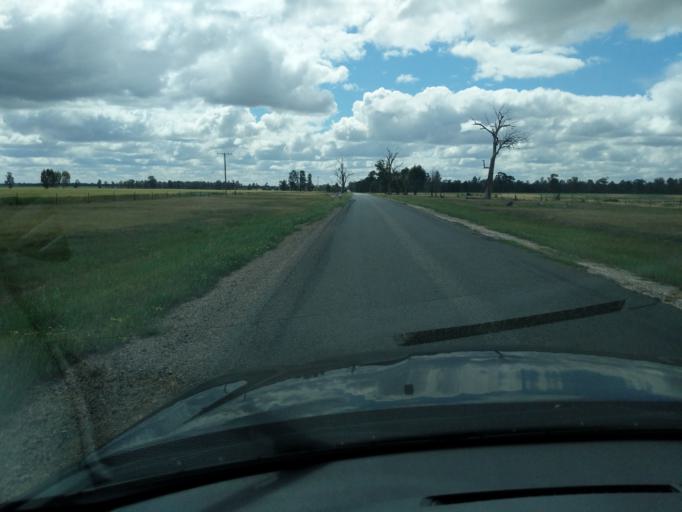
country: AU
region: New South Wales
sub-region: Coolamon
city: Coolamon
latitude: -34.8590
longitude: 146.8982
